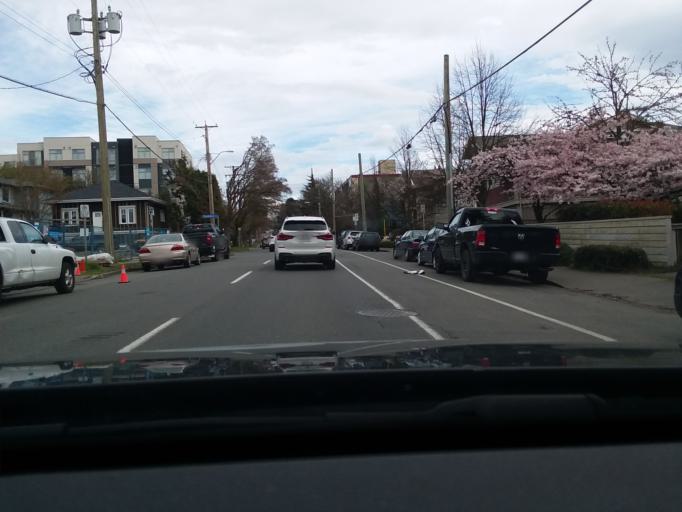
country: CA
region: British Columbia
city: Victoria
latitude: 48.4257
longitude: -123.3513
